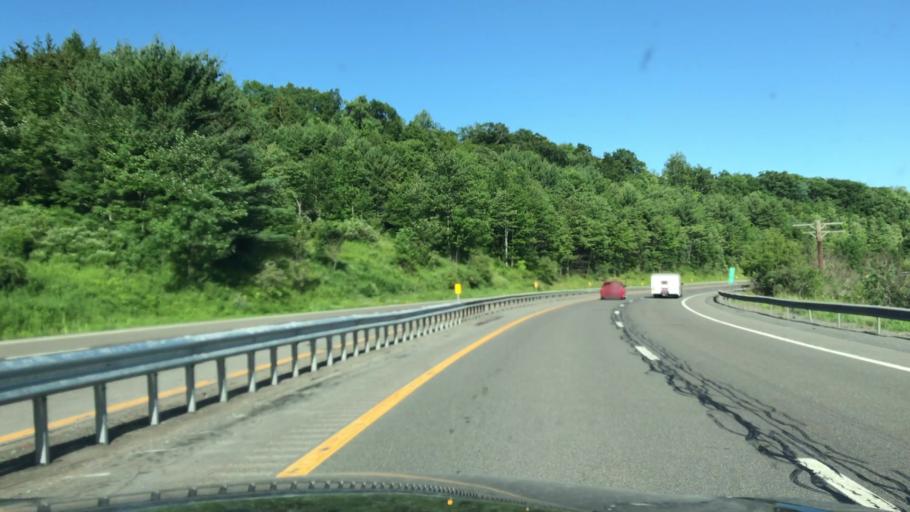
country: US
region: New York
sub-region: Broome County
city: Deposit
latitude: 42.0094
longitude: -75.3655
